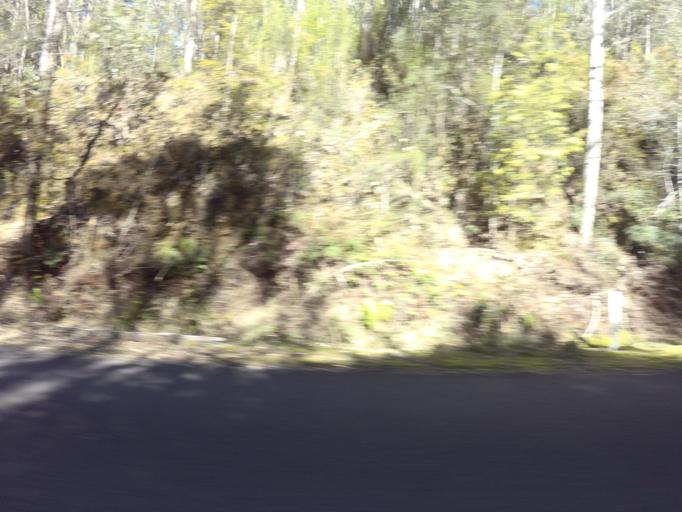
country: AU
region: Tasmania
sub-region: Huon Valley
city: Geeveston
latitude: -42.8240
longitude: 146.3312
